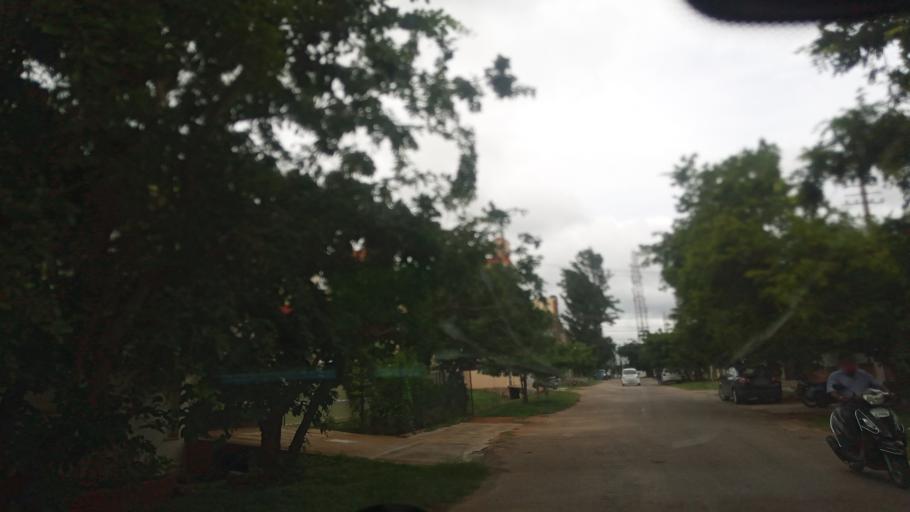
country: IN
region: Karnataka
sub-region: Mysore
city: Mysore
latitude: 12.2882
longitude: 76.6122
